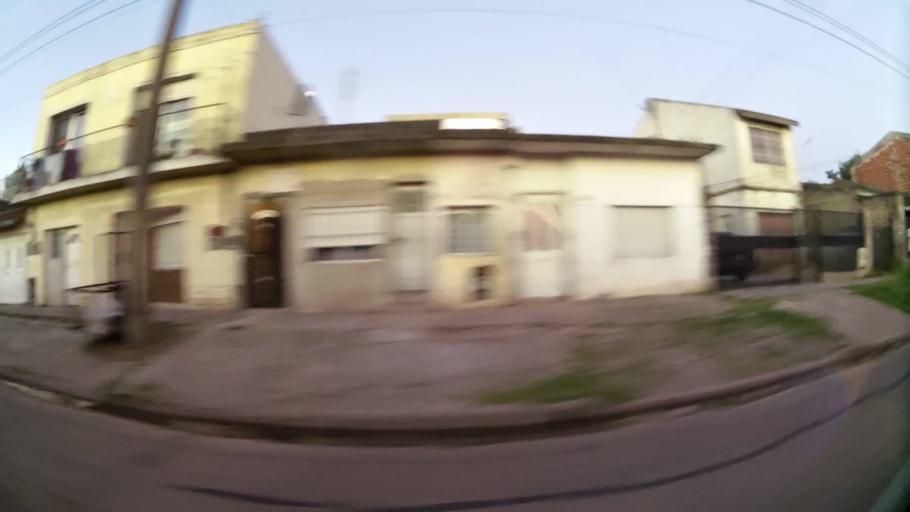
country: AR
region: Buenos Aires
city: San Justo
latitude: -34.7051
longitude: -58.6036
